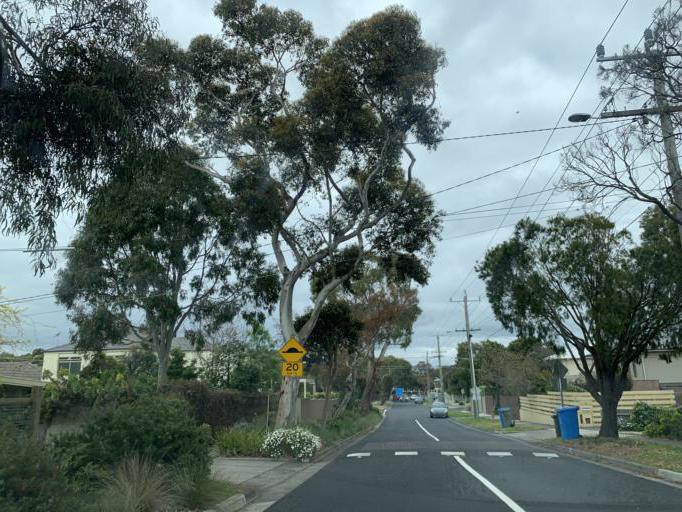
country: AU
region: Victoria
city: Beaumaris
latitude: -37.9820
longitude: 145.0312
